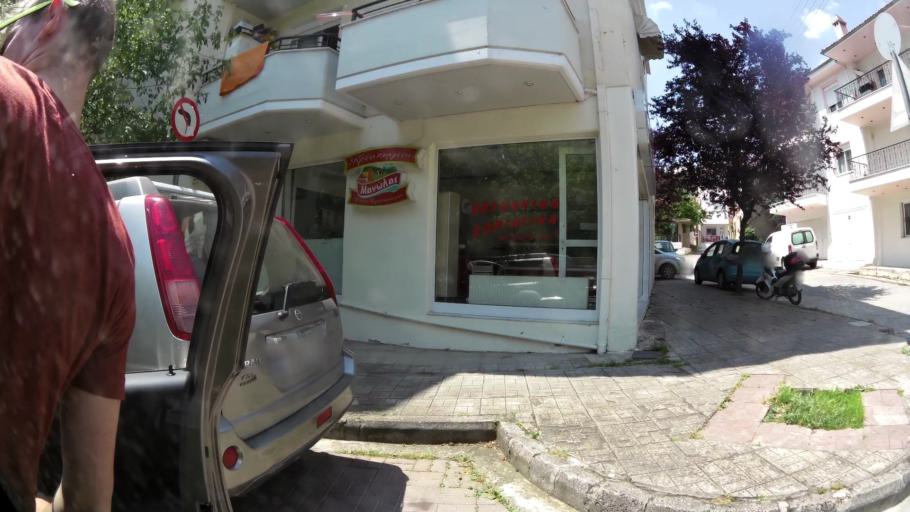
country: GR
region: West Macedonia
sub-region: Nomos Kozanis
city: Kozani
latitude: 40.2998
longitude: 21.7827
